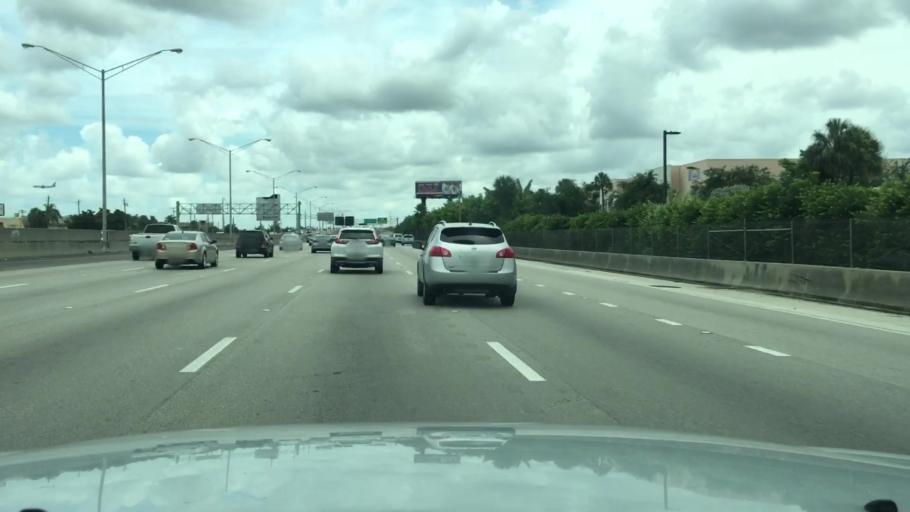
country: US
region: Florida
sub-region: Miami-Dade County
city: Virginia Gardens
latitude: 25.8171
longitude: -80.3219
